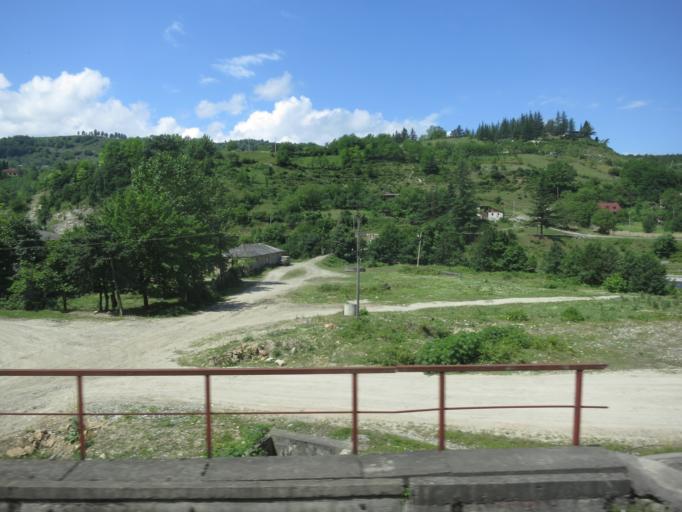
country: GE
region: Imereti
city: Kharagauli
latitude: 42.0253
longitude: 43.1994
